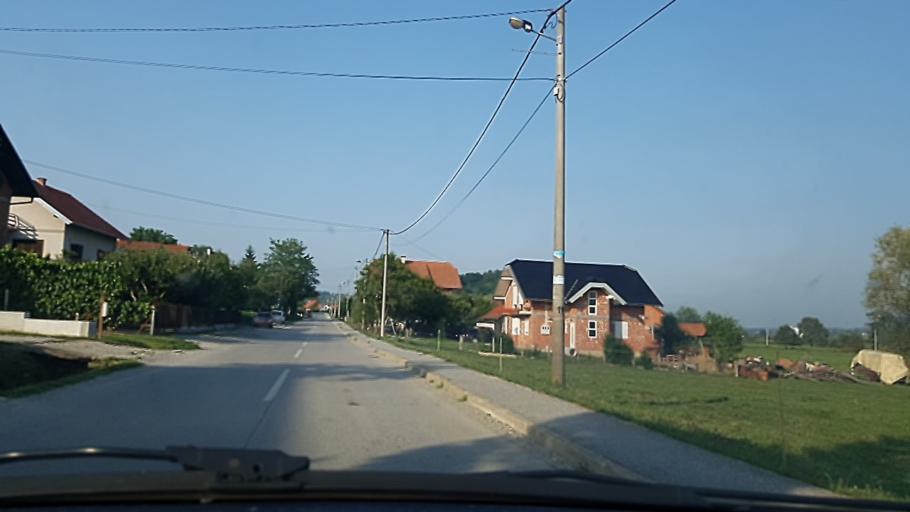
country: HR
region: Zagrebacka
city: Jakovlje
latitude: 45.9553
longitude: 15.8157
